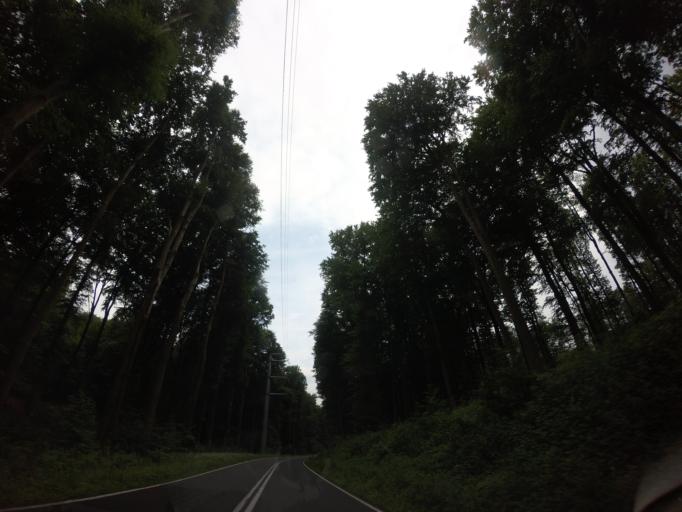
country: PL
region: West Pomeranian Voivodeship
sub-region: Powiat drawski
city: Wierzchowo
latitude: 53.4198
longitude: 16.2018
